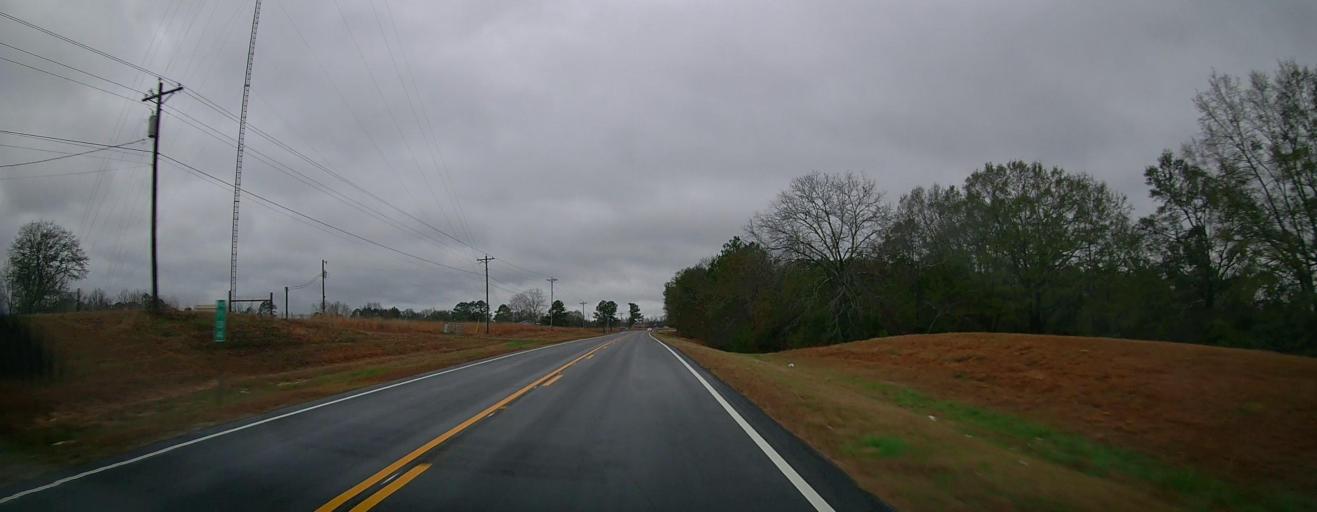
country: US
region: Alabama
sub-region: Chilton County
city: Thorsby
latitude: 32.7833
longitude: -86.8971
